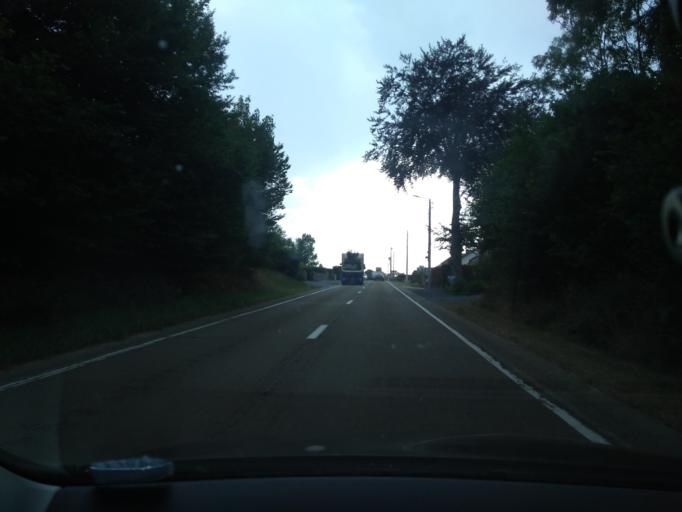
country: BE
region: Wallonia
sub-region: Province du Luxembourg
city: Sainte-Ode
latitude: 50.0359
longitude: 5.5447
